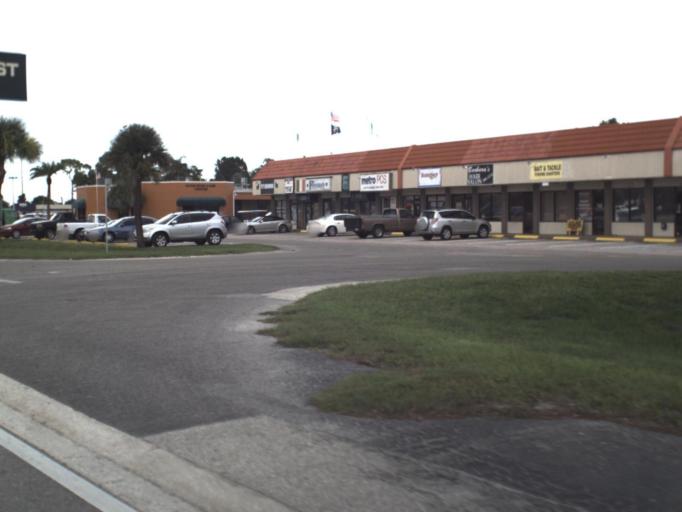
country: US
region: Florida
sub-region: Sarasota County
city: Venice
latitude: 27.0918
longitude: -82.4330
